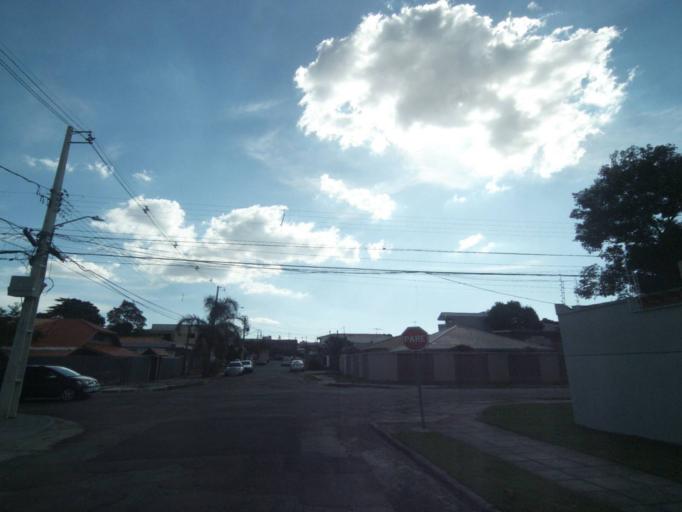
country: BR
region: Parana
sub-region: Pinhais
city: Pinhais
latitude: -25.4609
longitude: -49.2102
